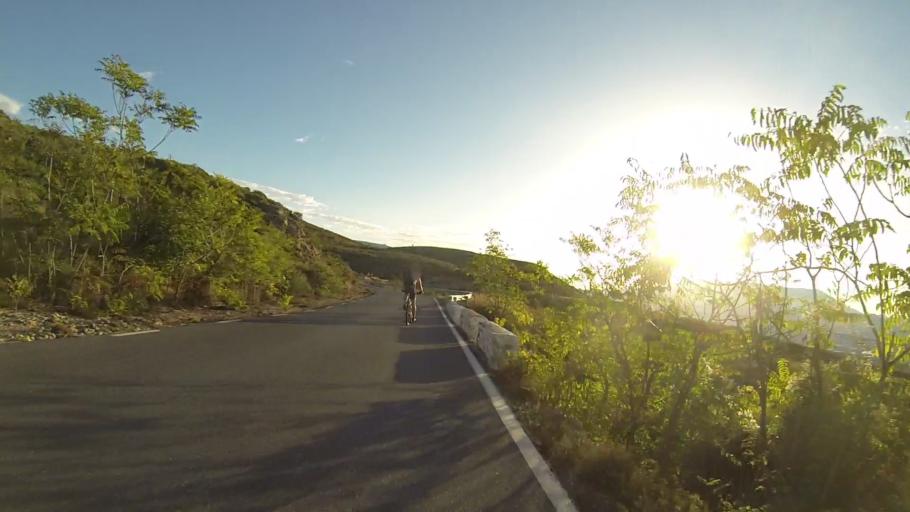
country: ES
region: Andalusia
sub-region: Provincia de Granada
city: Valor
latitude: 36.9782
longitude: -3.1306
